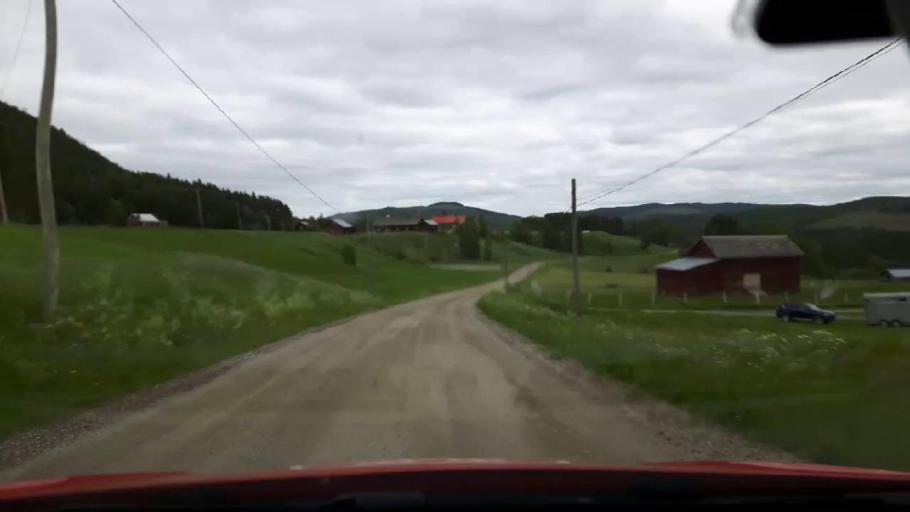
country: SE
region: Jaemtland
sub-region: Ragunda Kommun
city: Hammarstrand
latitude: 63.1662
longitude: 16.2141
